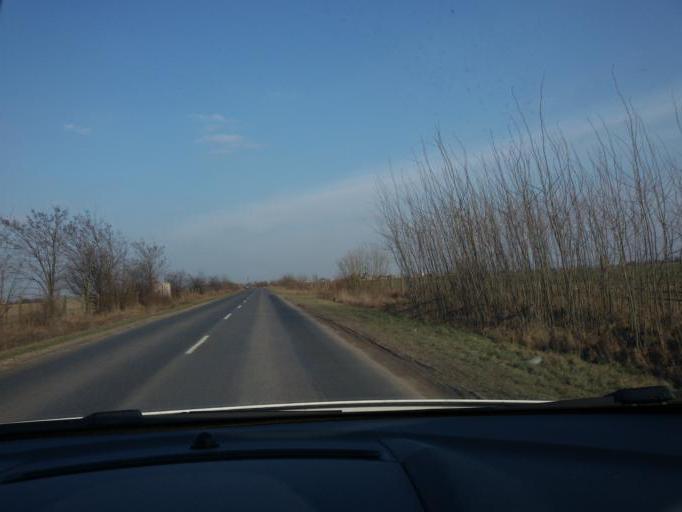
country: PL
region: Greater Poland Voivodeship
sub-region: Powiat gostynski
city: Krobia
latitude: 51.7686
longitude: 16.9470
